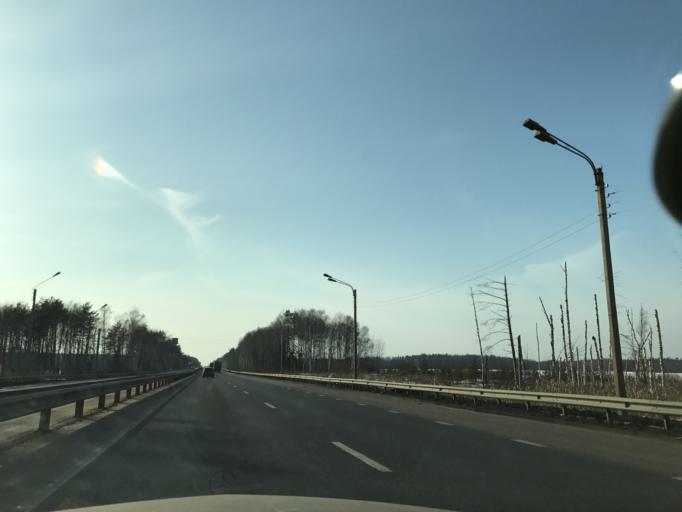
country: RU
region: Vladimir
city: Nikologory
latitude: 56.2366
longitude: 41.9387
